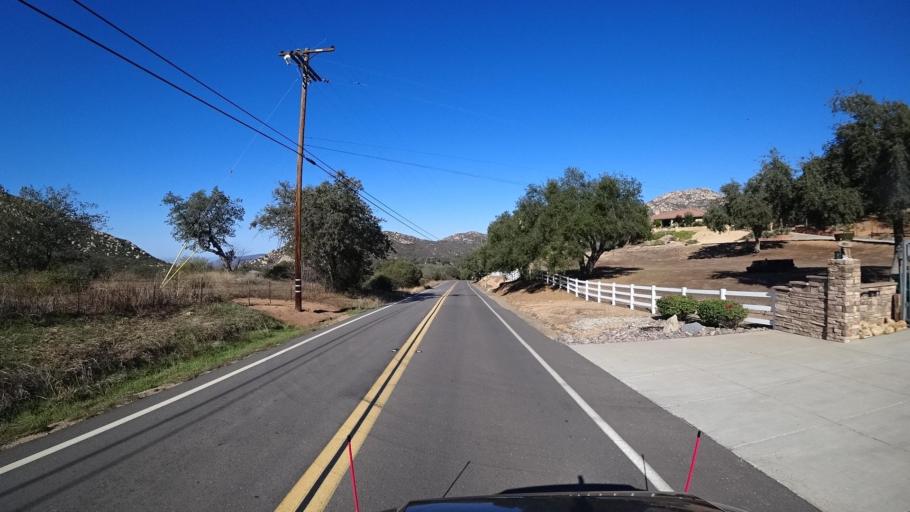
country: US
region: California
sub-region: San Diego County
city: Jamul
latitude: 32.6771
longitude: -116.7442
